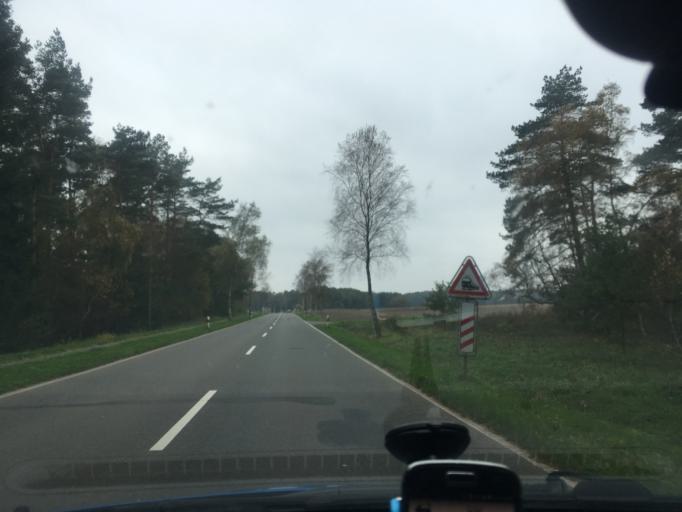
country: DE
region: Lower Saxony
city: Soderstorf
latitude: 53.1160
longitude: 10.0864
